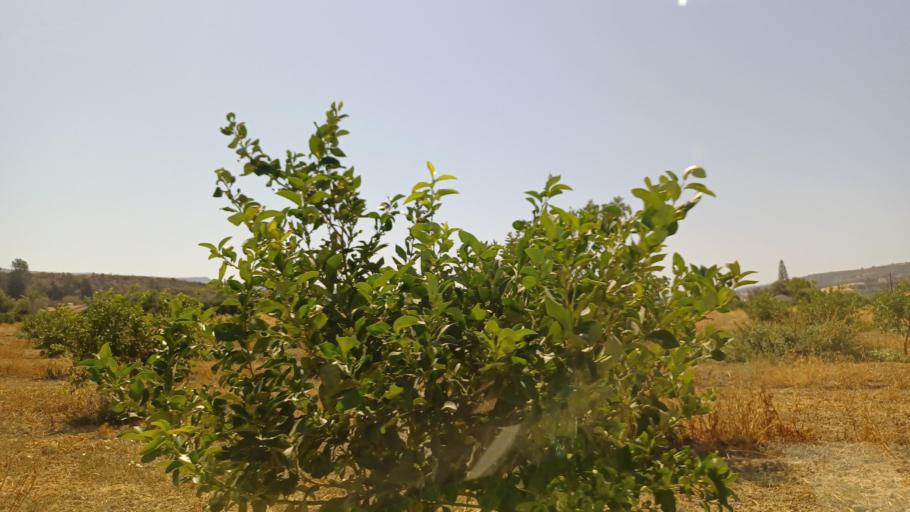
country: CY
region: Pafos
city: Polis
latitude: 35.0113
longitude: 32.4325
